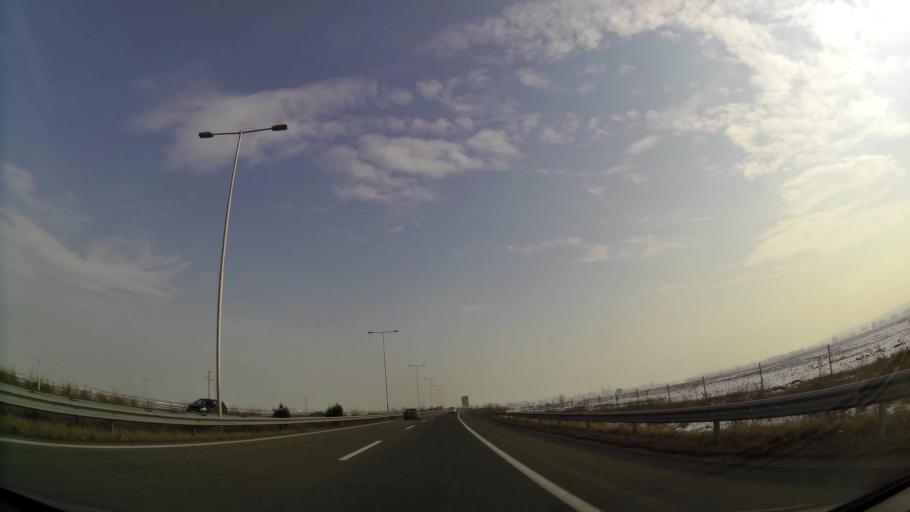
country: MK
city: Creshevo
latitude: 42.0319
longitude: 21.5002
